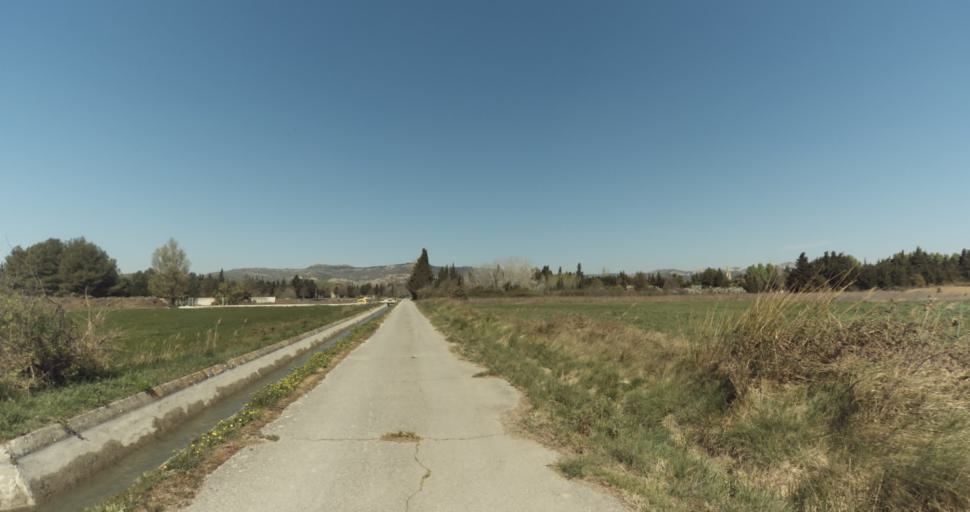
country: FR
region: Provence-Alpes-Cote d'Azur
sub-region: Departement des Bouches-du-Rhone
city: Pelissanne
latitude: 43.6247
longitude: 5.1461
